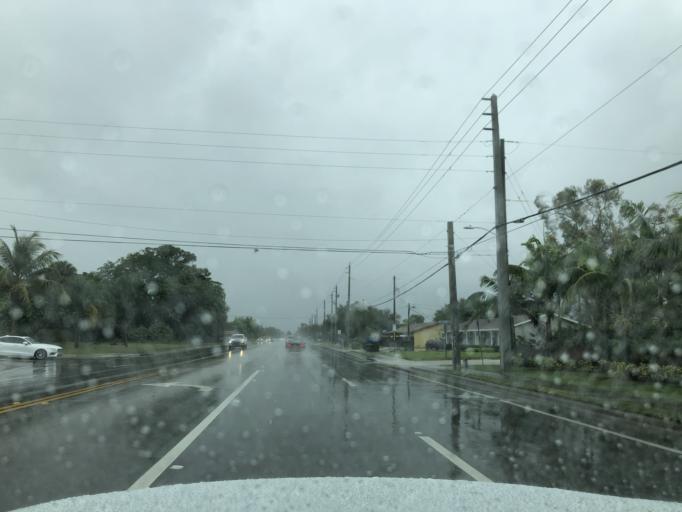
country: US
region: Florida
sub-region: Palm Beach County
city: Haverhill
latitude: 26.6872
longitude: -80.1200
